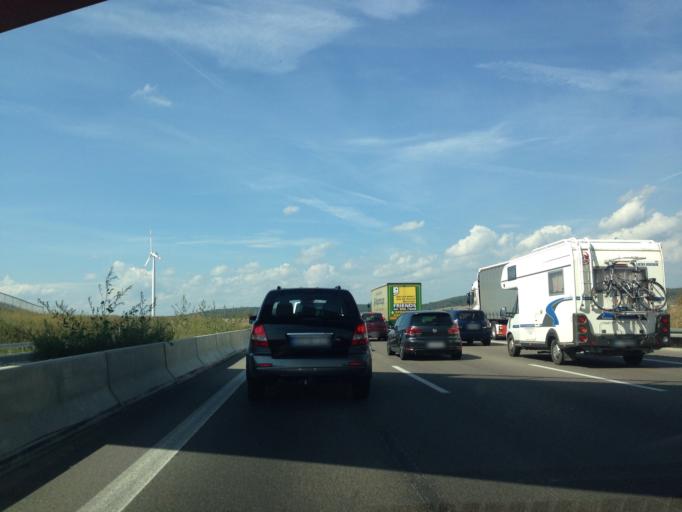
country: DE
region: Baden-Wuerttemberg
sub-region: Tuebingen Region
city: Dornstadt
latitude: 48.4772
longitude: 9.8800
